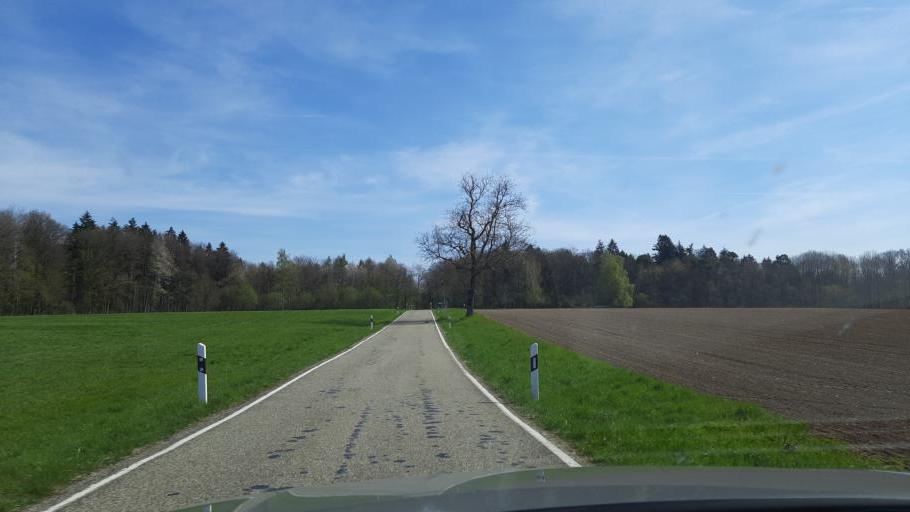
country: DE
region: Baden-Wuerttemberg
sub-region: Regierungsbezirk Stuttgart
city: Widdern
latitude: 49.2740
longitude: 9.4185
